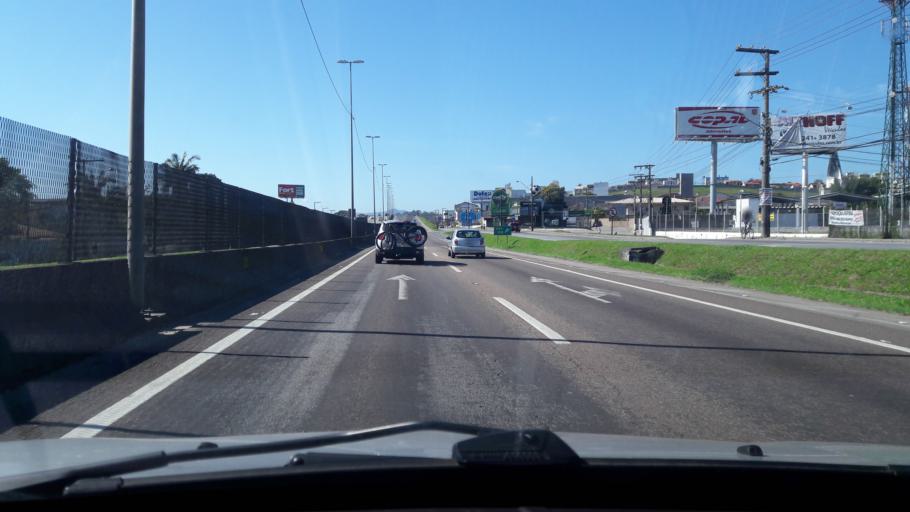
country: BR
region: Santa Catarina
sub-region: Biguacu
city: Biguacu
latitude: -27.5355
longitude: -48.6283
